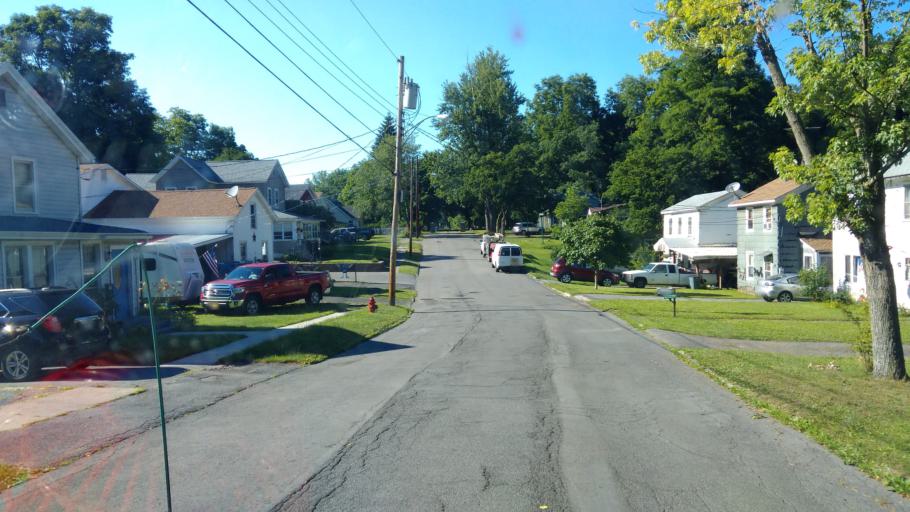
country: US
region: New York
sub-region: Wayne County
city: Lyons
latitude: 43.0722
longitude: -76.9878
